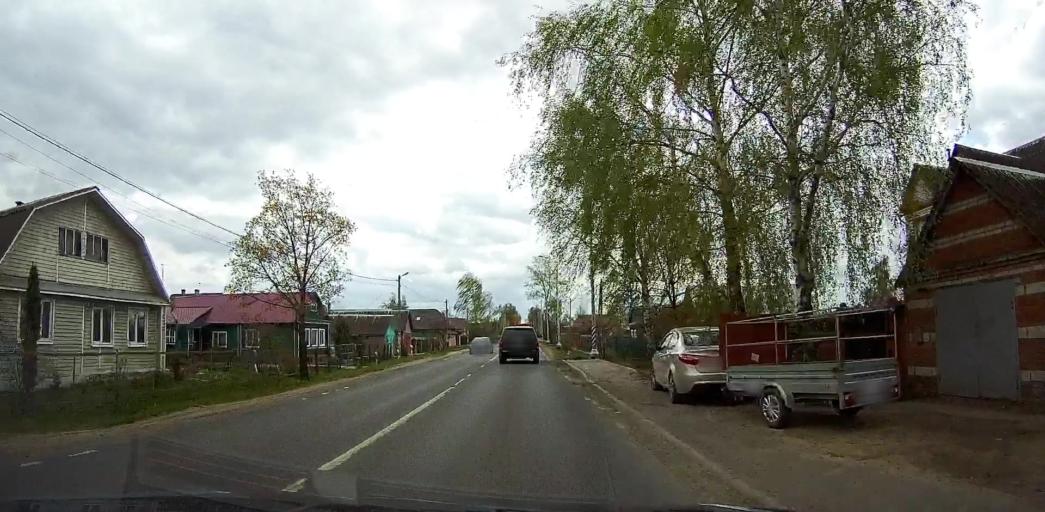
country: RU
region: Moskovskaya
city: Beloozerskiy
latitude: 55.4639
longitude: 38.4201
